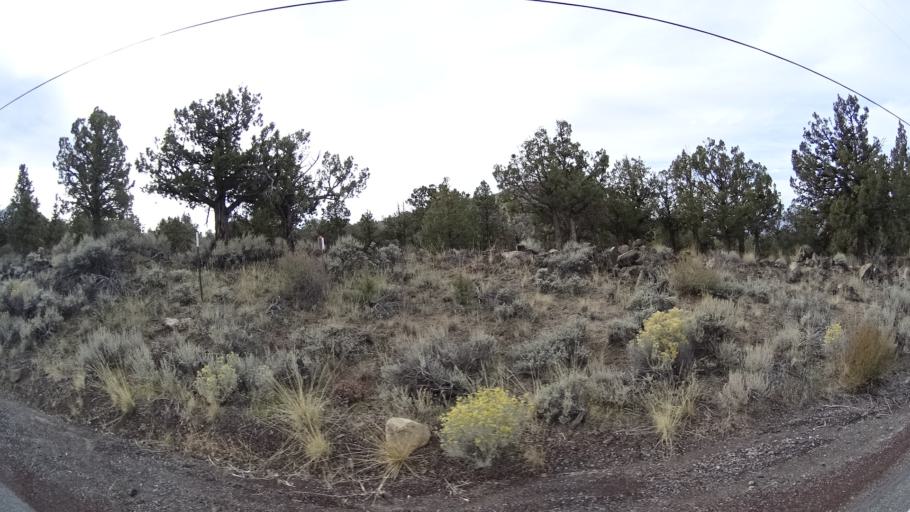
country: US
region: California
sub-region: Siskiyou County
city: Weed
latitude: 41.5521
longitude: -122.2507
